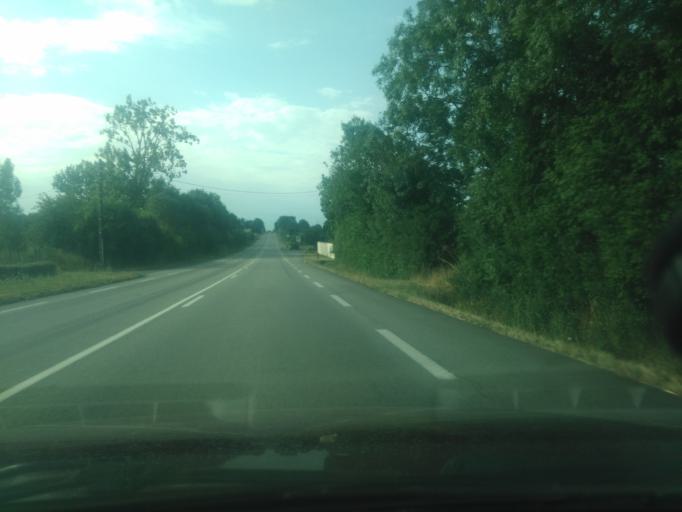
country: FR
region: Pays de la Loire
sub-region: Departement de la Vendee
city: Chantonnay
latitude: 46.7115
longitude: -1.0666
